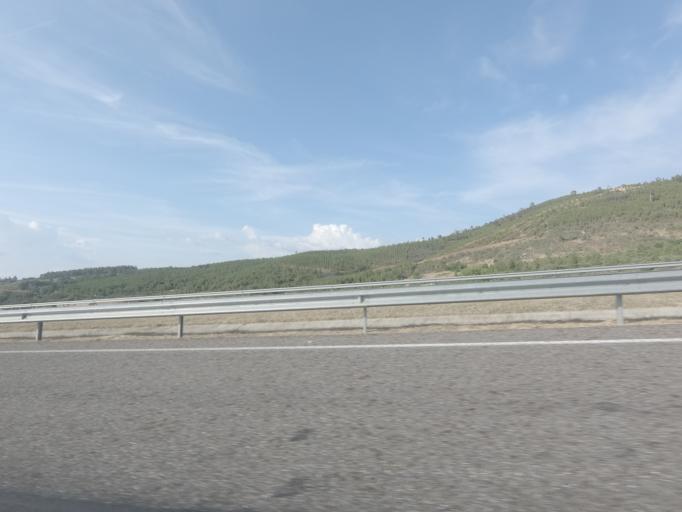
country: ES
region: Galicia
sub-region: Provincia de Ourense
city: Oimbra
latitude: 41.8645
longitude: -7.4291
